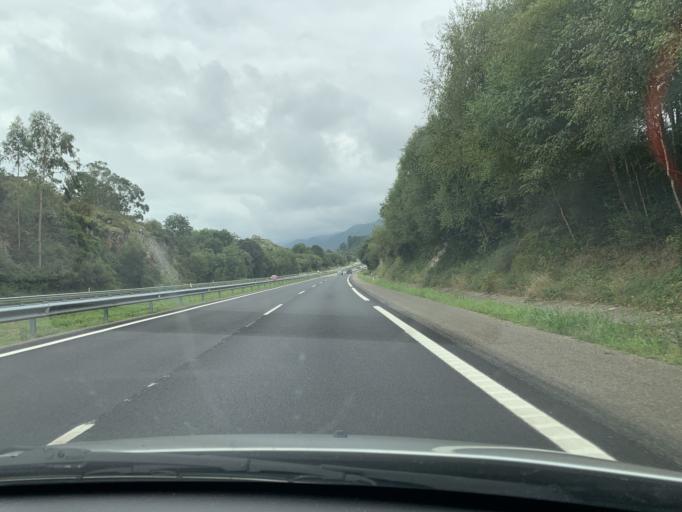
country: ES
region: Asturias
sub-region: Province of Asturias
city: Llanes
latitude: 43.4189
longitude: -4.7928
